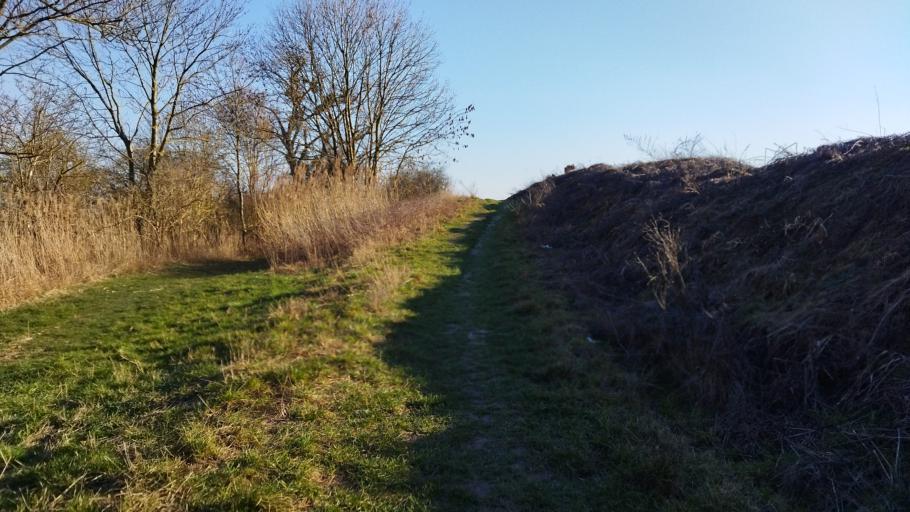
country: DE
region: Rheinland-Pfalz
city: Waldsee
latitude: 49.4128
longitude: 8.4510
